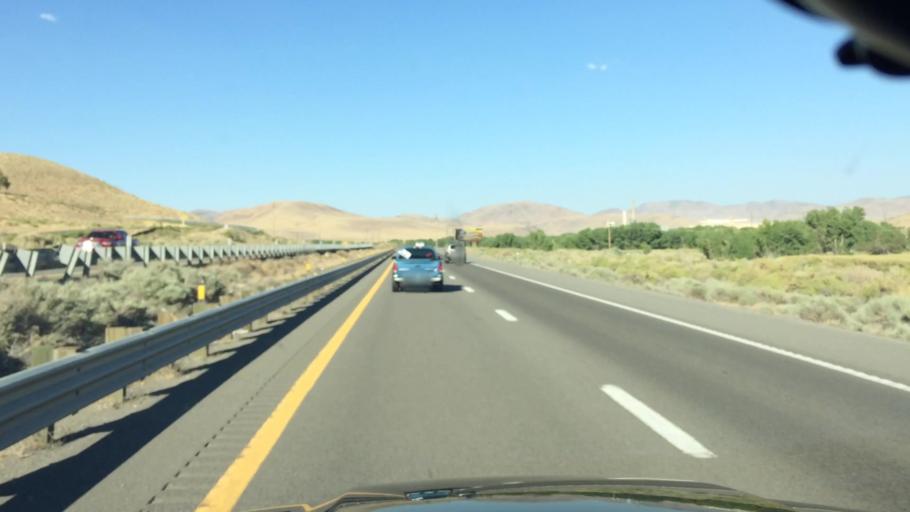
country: US
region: Nevada
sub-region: Washoe County
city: Spanish Springs
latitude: 39.5627
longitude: -119.5452
